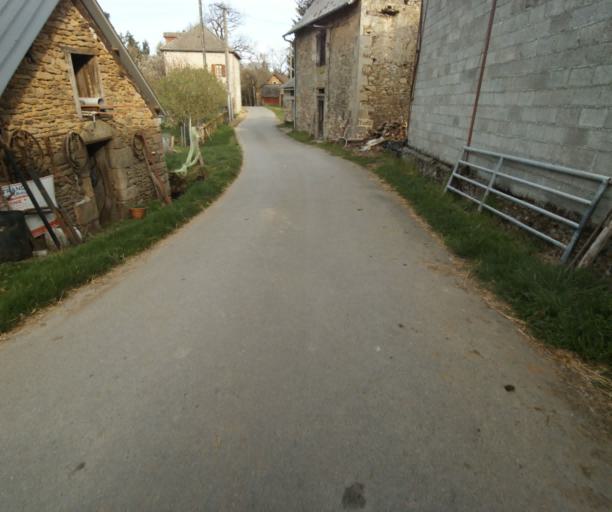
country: FR
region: Limousin
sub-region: Departement de la Correze
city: Chamboulive
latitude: 45.4457
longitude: 1.7750
